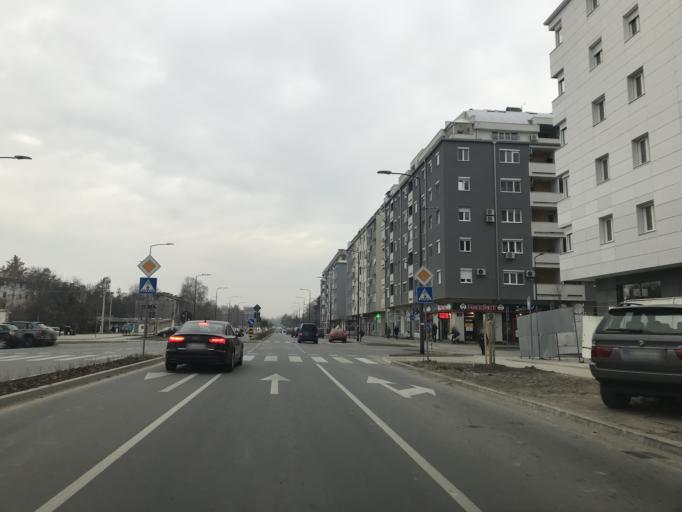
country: RS
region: Autonomna Pokrajina Vojvodina
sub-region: Juznobacki Okrug
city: Novi Sad
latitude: 45.2477
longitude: 19.7995
